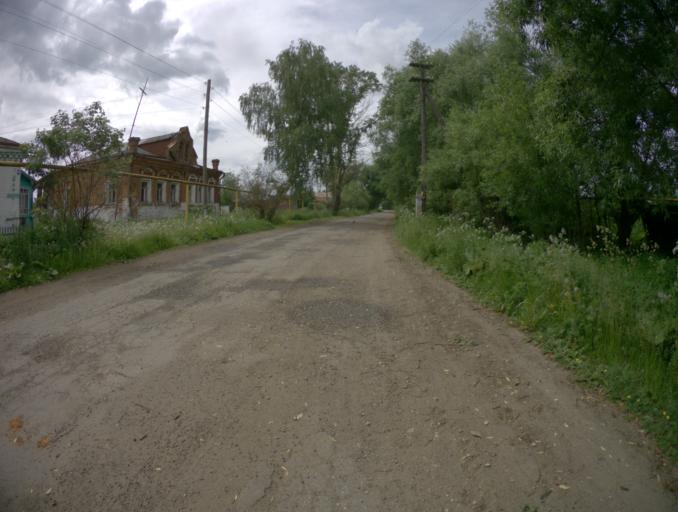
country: RU
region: Vladimir
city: Stavrovo
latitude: 56.2348
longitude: 39.8864
